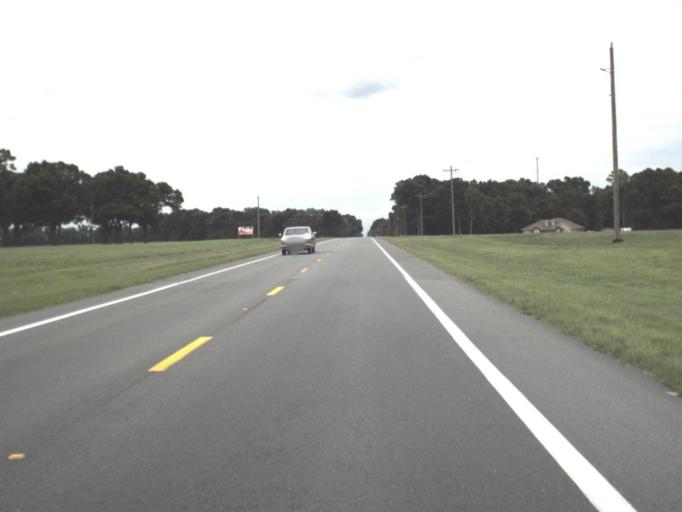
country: US
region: Florida
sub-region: Suwannee County
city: Wellborn
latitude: 30.0056
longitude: -82.8526
